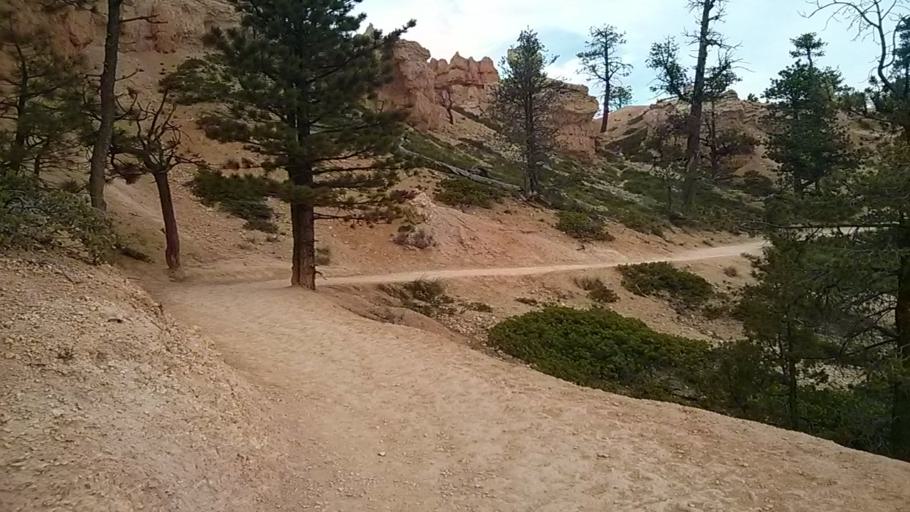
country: US
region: Utah
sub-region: Garfield County
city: Panguitch
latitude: 37.6260
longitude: -112.1591
